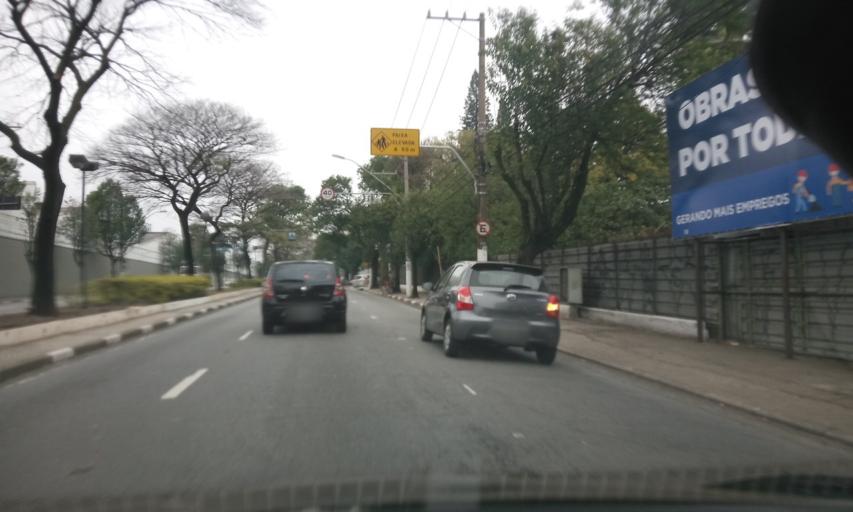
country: BR
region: Sao Paulo
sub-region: Santo Andre
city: Santo Andre
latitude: -23.6624
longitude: -46.5702
